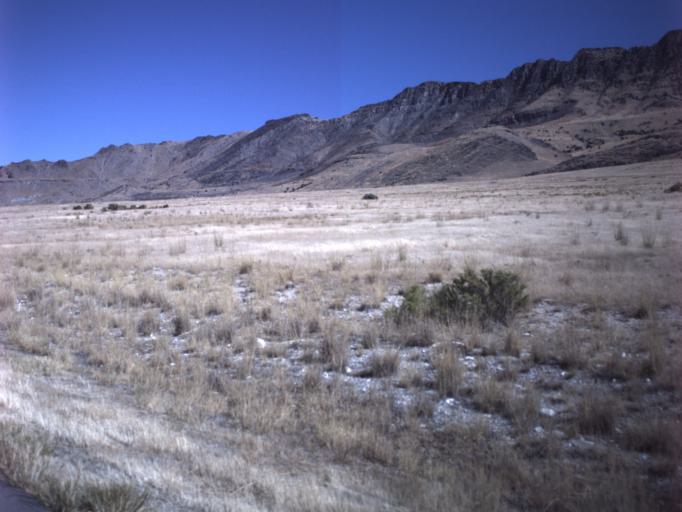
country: US
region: Utah
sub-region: Tooele County
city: Grantsville
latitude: 40.6956
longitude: -112.6671
